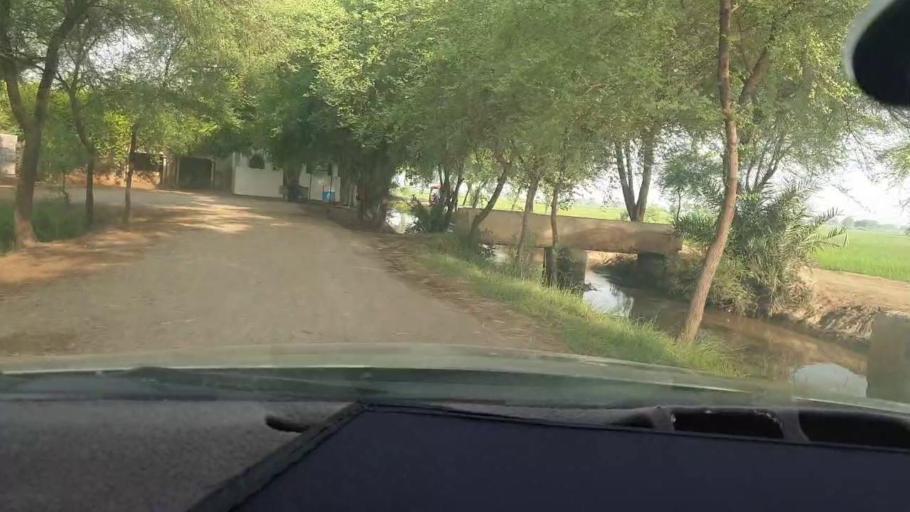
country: PK
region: Sindh
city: Jacobabad
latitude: 28.3095
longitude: 68.4120
